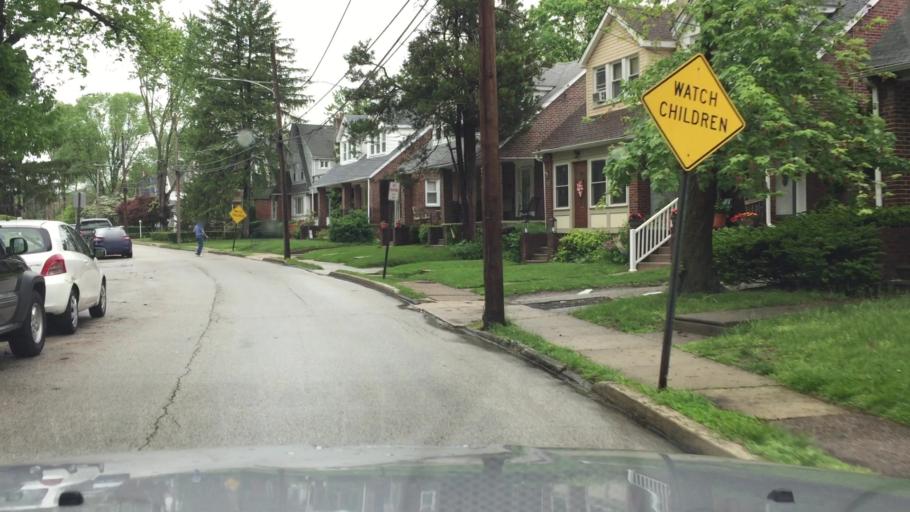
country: US
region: Pennsylvania
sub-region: Delaware County
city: Drexel Hill
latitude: 39.9717
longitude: -75.3046
